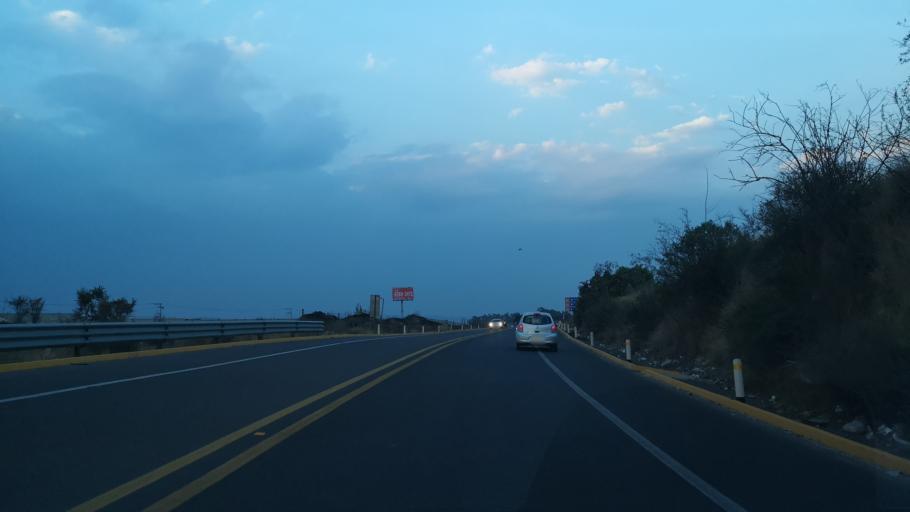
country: MX
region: Puebla
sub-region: Huejotzingo
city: Los Encinos
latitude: 19.1695
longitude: -98.3771
